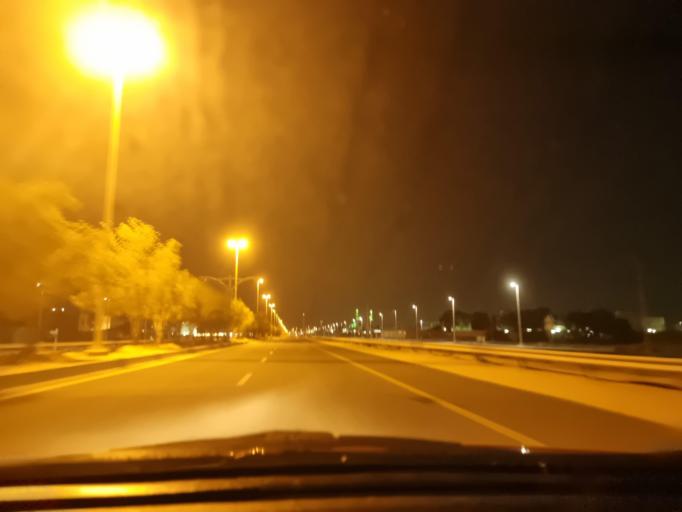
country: AE
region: Abu Dhabi
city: Abu Dhabi
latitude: 24.3697
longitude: 54.7042
